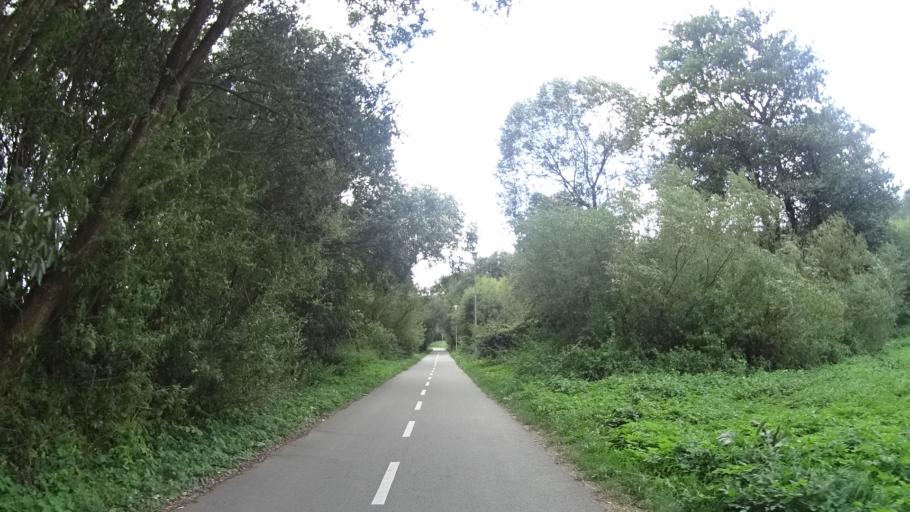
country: CZ
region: Pardubicky
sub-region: Okres Usti nad Orlici
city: Usti nad Orlici
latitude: 49.9801
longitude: 16.3862
